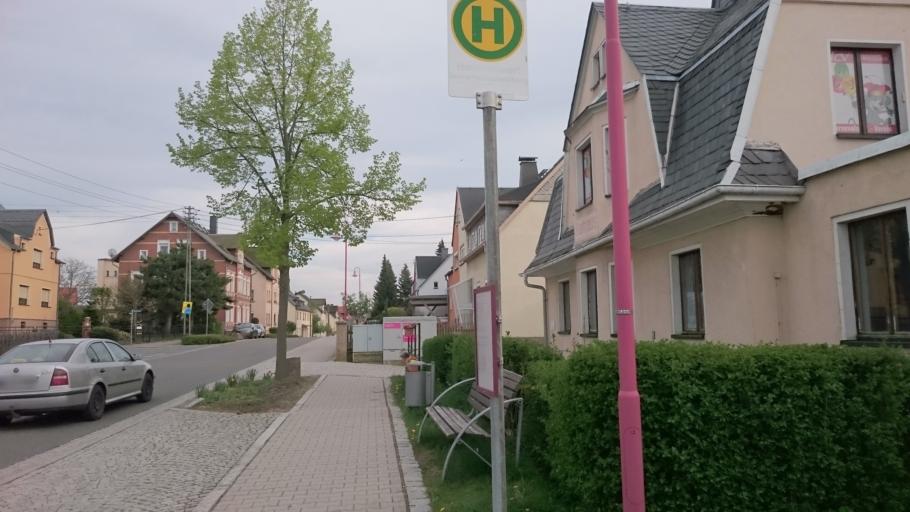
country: DE
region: Saxony
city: Lichtenstein
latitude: 50.7307
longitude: 12.6373
